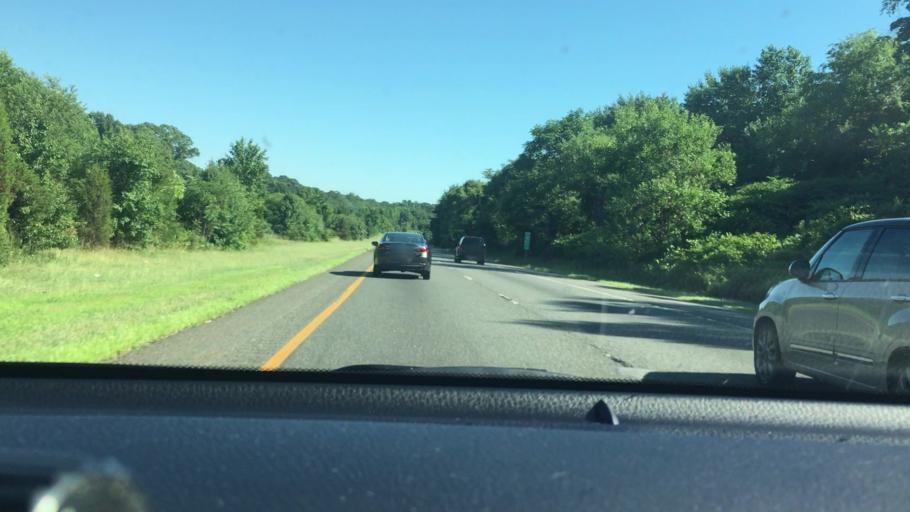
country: US
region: New Jersey
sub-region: Camden County
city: Blackwood
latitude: 39.8114
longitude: -75.1061
